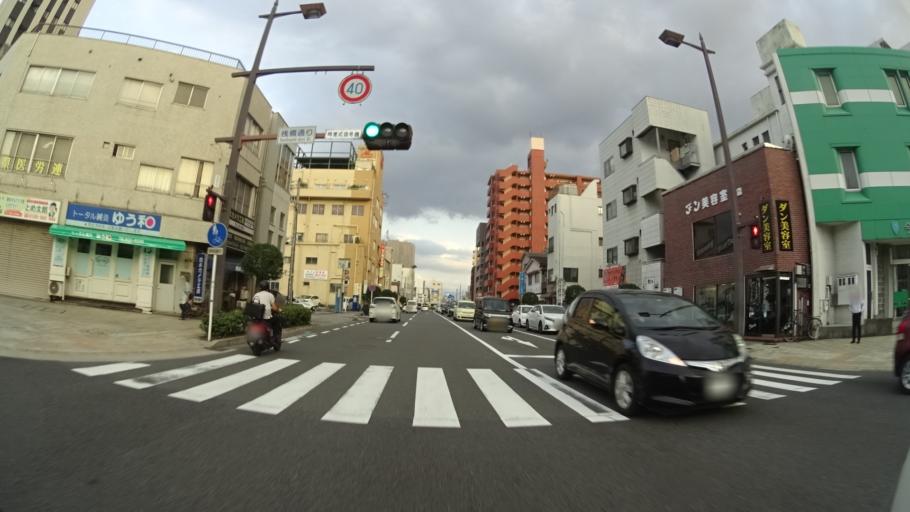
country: JP
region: Kagoshima
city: Kagoshima-shi
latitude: 31.5977
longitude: 130.5587
